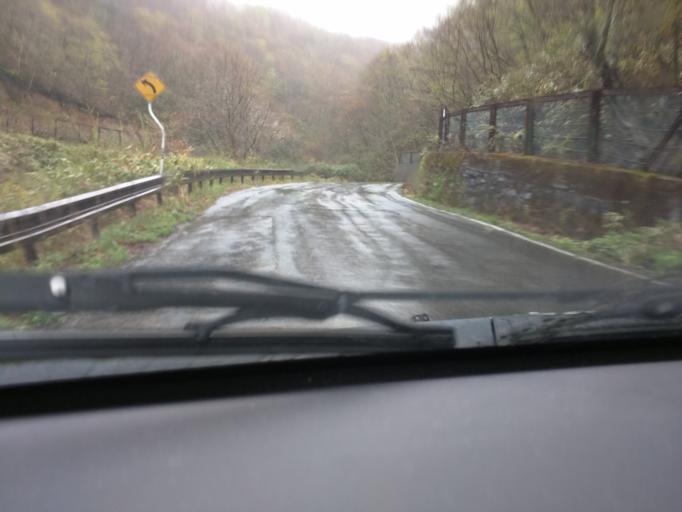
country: JP
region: Fukushima
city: Inawashiro
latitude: 37.6622
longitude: 140.2572
